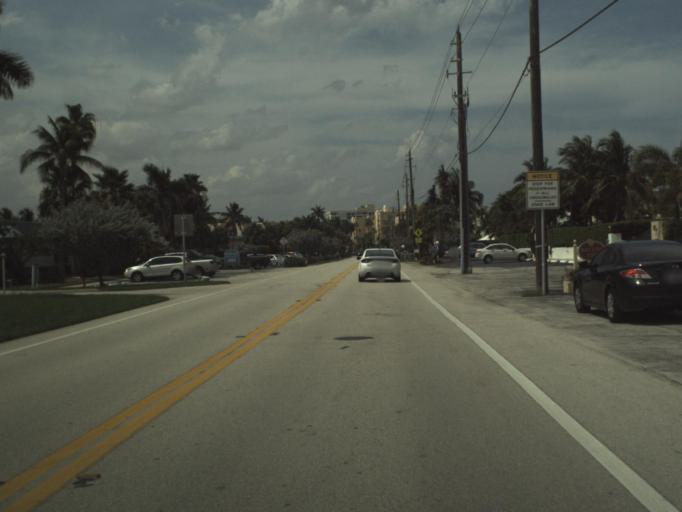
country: US
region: Florida
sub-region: Broward County
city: Hillsboro Beach
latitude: 26.3007
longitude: -80.0782
